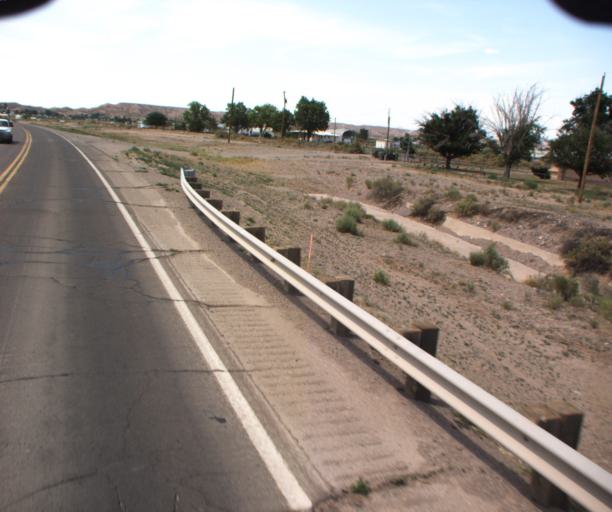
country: US
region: Arizona
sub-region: Greenlee County
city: Clifton
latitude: 32.7377
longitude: -109.0934
